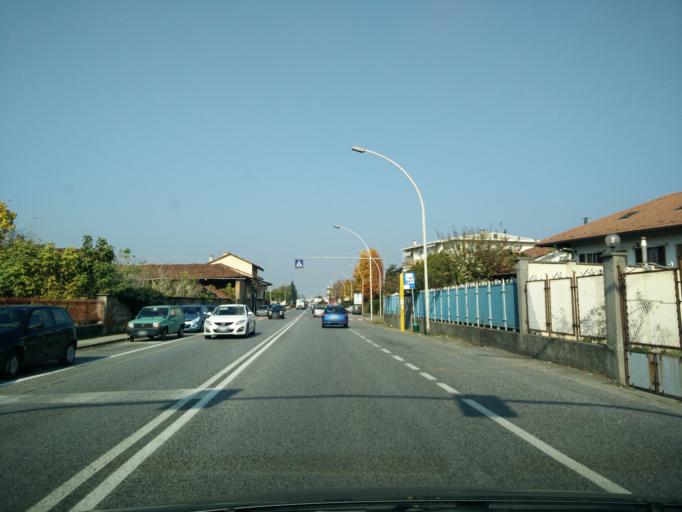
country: IT
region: Piedmont
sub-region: Provincia di Torino
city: Caselle Torinese
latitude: 45.1763
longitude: 7.6505
